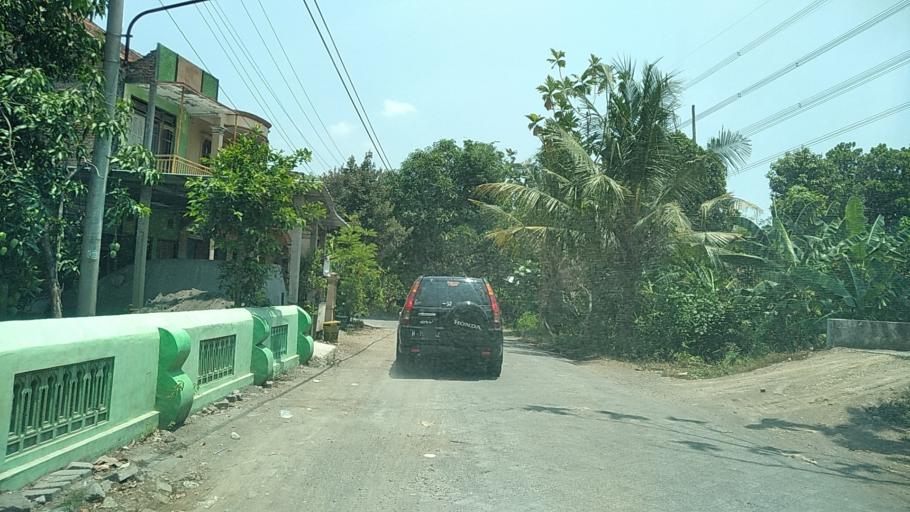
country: ID
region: Central Java
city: Mranggen
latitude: -7.0076
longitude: 110.4884
